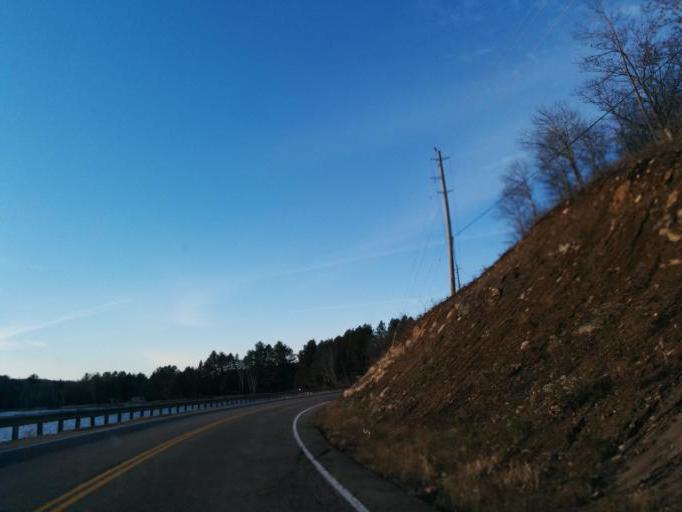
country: CA
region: Ontario
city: Bancroft
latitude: 45.0233
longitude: -78.3803
